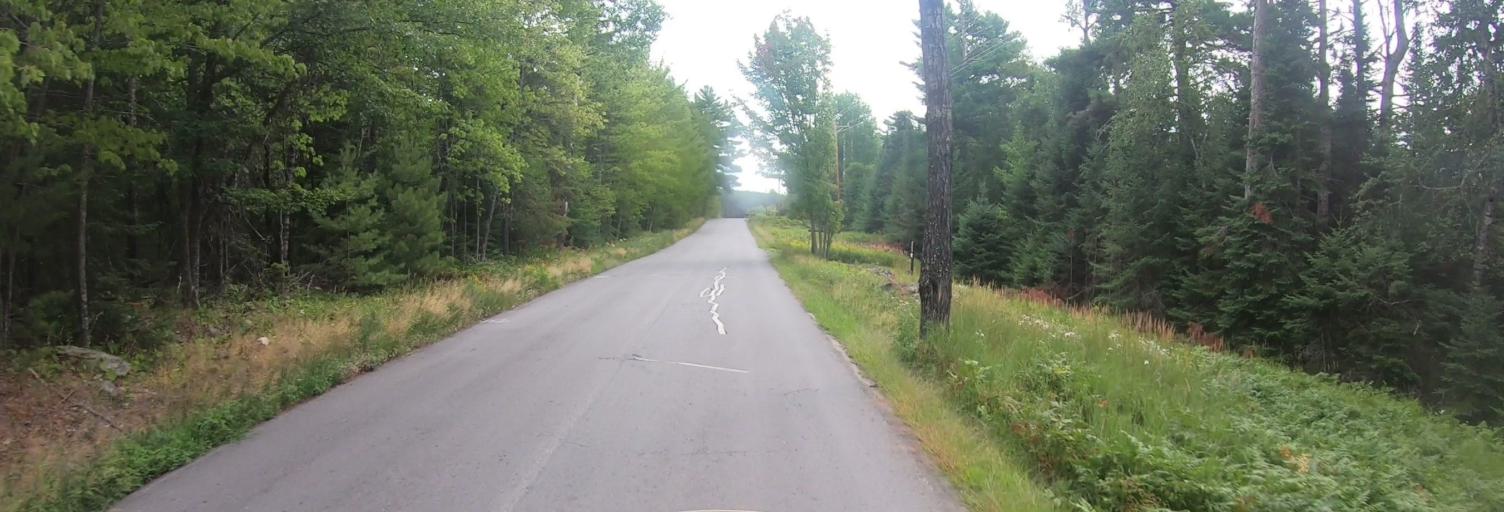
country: US
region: Minnesota
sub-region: Saint Louis County
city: Mountain Iron
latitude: 47.9556
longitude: -92.6458
